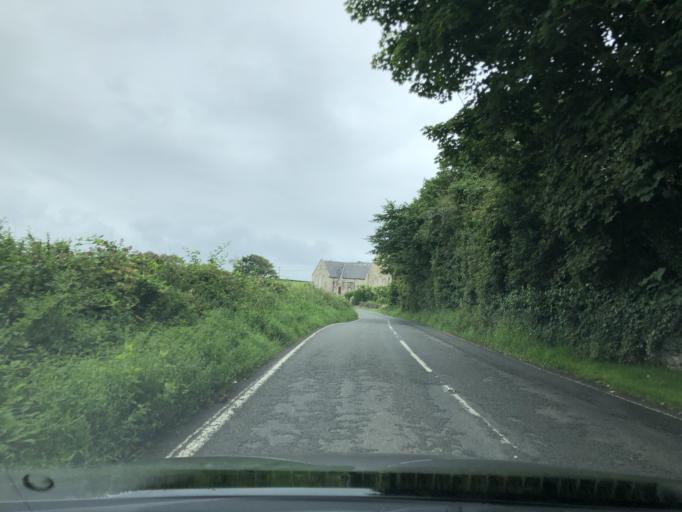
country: GB
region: Northern Ireland
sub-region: Down District
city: Dundrum
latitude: 54.2545
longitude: -5.7705
